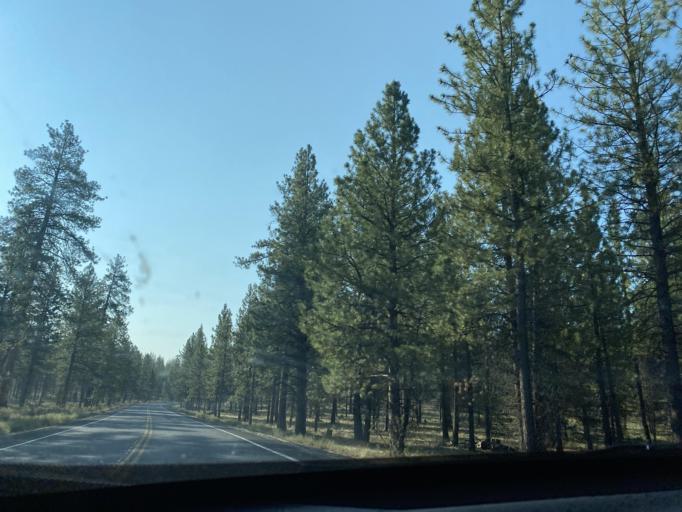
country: US
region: Oregon
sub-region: Deschutes County
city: La Pine
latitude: 43.7113
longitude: -121.4101
